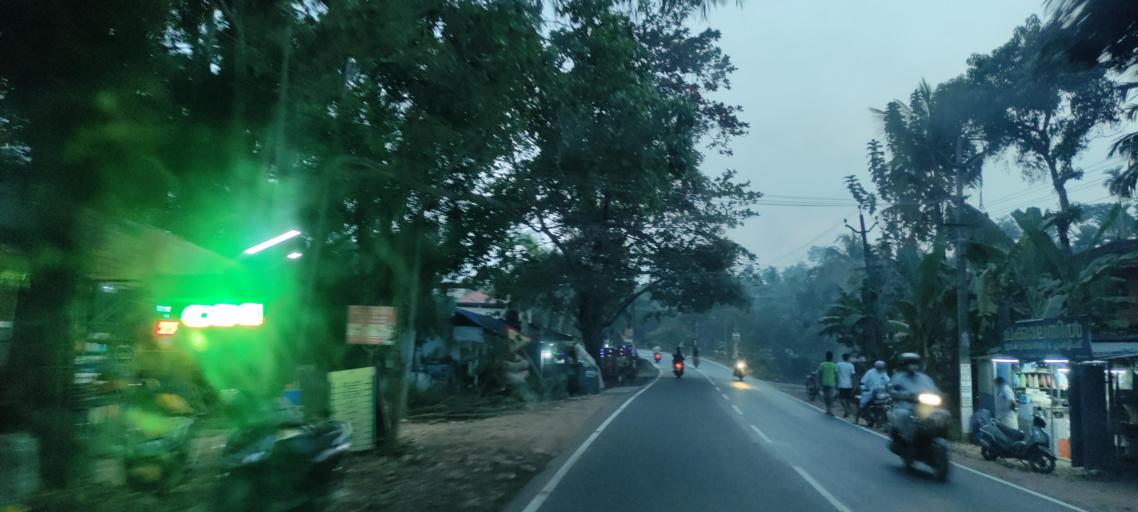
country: IN
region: Kerala
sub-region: Alappuzha
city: Mavelikara
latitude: 9.3284
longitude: 76.4625
